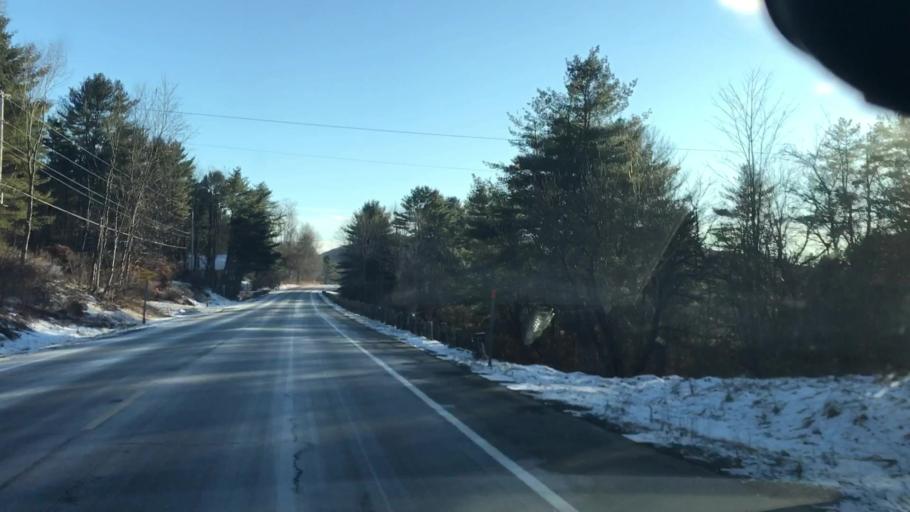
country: US
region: New Hampshire
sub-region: Grafton County
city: Lyme Town Offices
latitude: 43.8587
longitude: -72.1553
